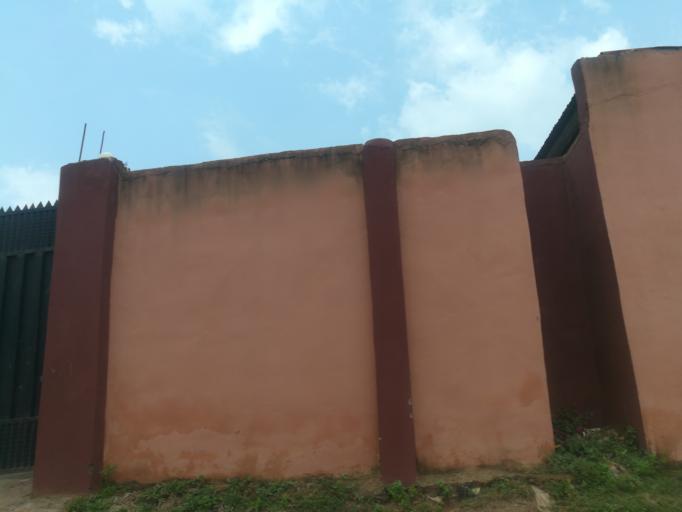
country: NG
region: Oyo
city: Moniya
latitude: 7.4534
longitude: 3.9579
